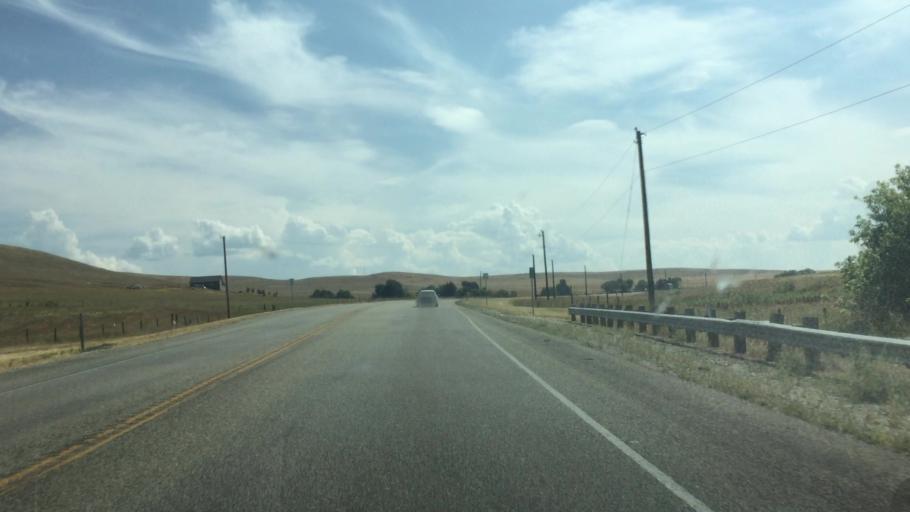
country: US
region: Utah
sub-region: Cache County
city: Mendon
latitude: 41.7938
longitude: -112.0362
